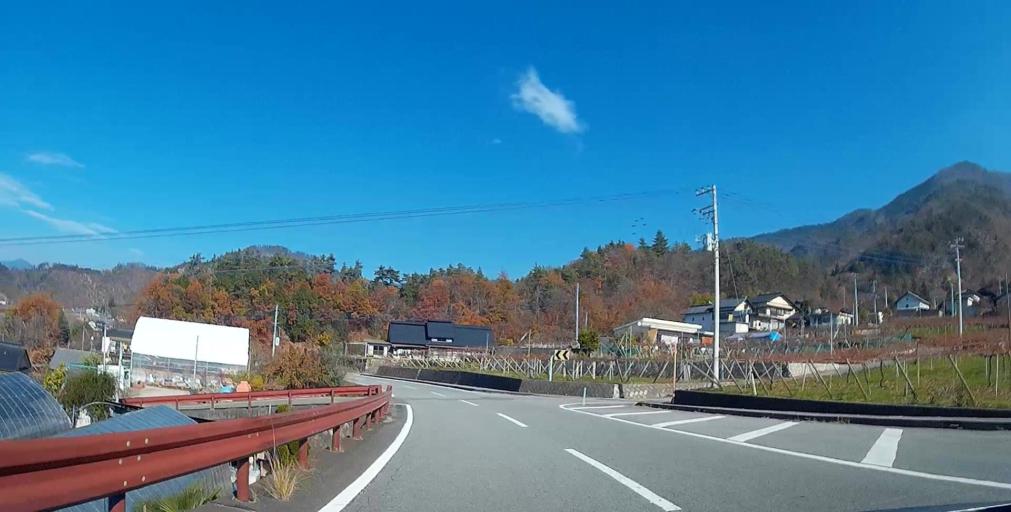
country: JP
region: Yamanashi
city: Enzan
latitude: 35.6798
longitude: 138.7488
